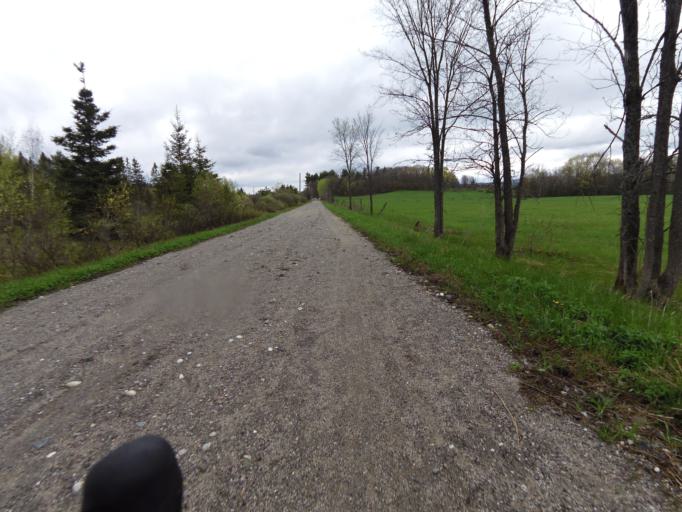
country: CA
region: Quebec
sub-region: Outaouais
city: Wakefield
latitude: 45.5909
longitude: -75.9026
